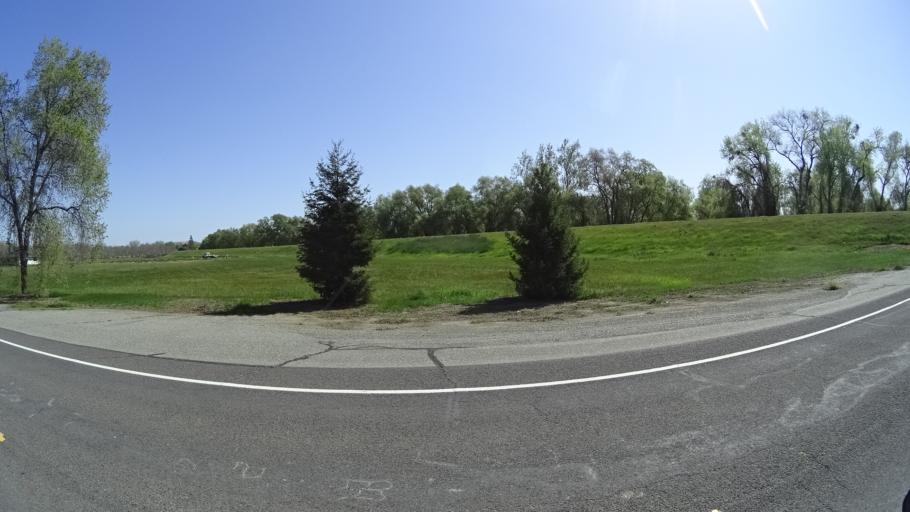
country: US
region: California
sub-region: Glenn County
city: Willows
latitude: 39.4537
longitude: -122.0174
